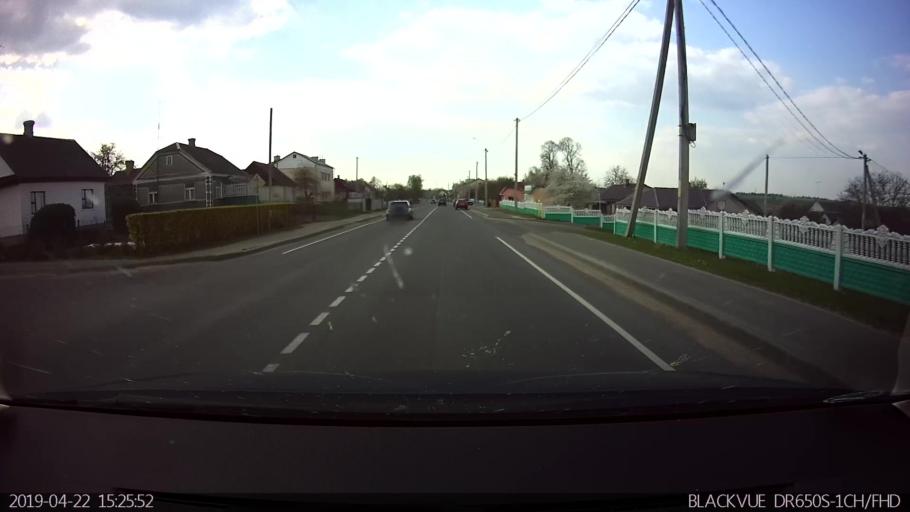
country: BY
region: Brest
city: Vysokaye
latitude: 52.3660
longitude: 23.3902
